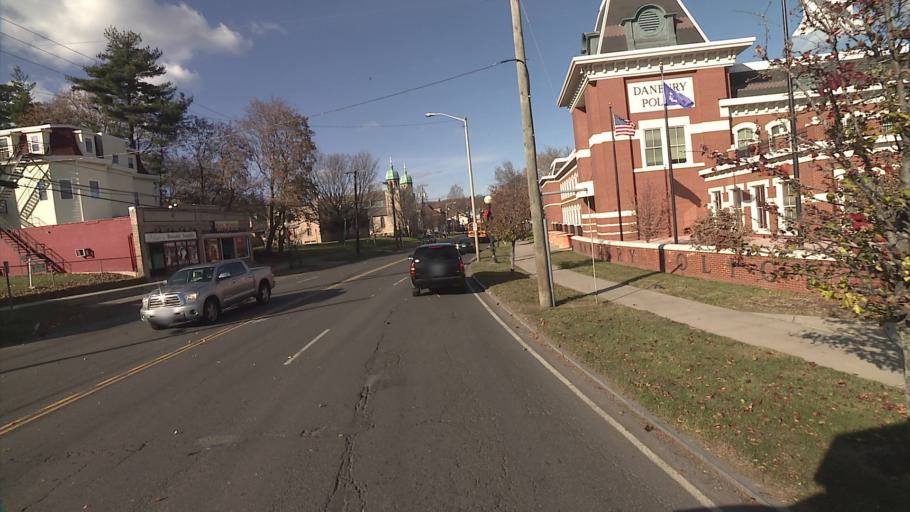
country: US
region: Connecticut
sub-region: Fairfield County
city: Danbury
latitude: 41.3997
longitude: -73.4580
